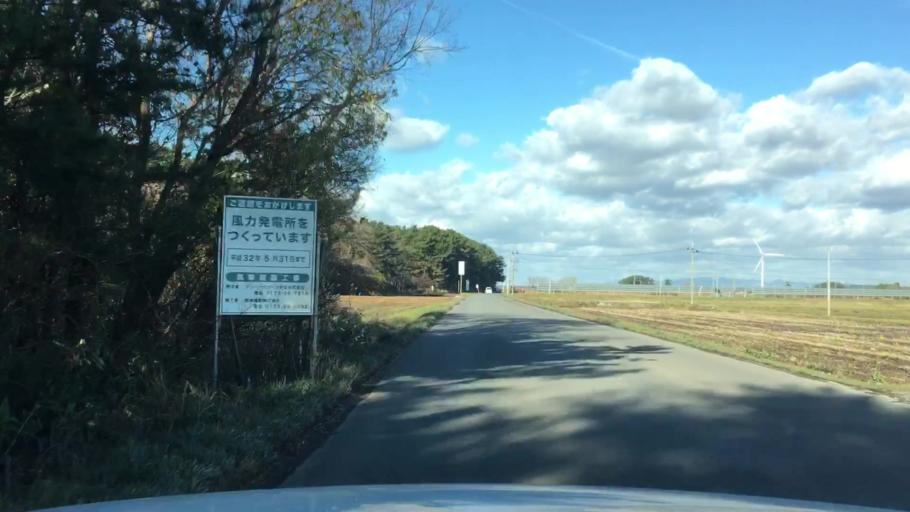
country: JP
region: Aomori
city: Shimokizukuri
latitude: 40.8469
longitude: 140.2998
